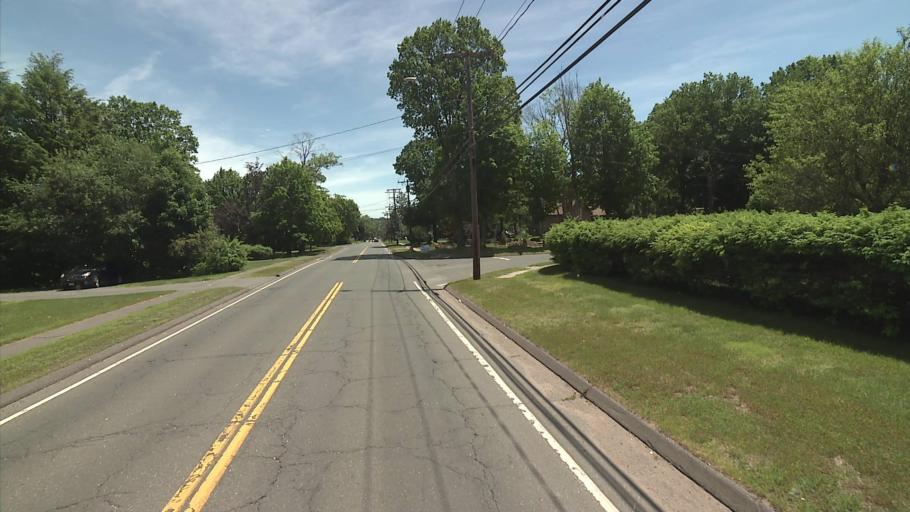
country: US
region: Connecticut
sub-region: Hartford County
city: Plainville
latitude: 41.5970
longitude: -72.8583
